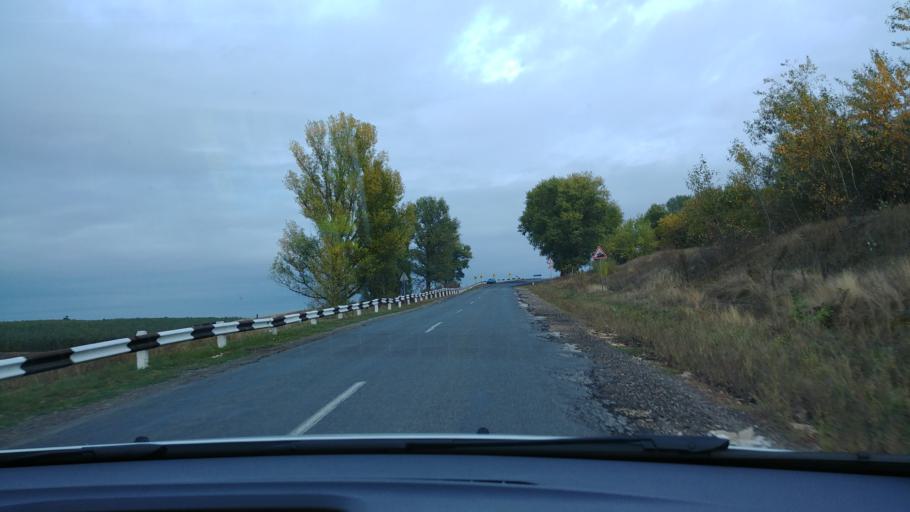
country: MD
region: Rezina
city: Rezina
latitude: 47.7588
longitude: 28.8827
